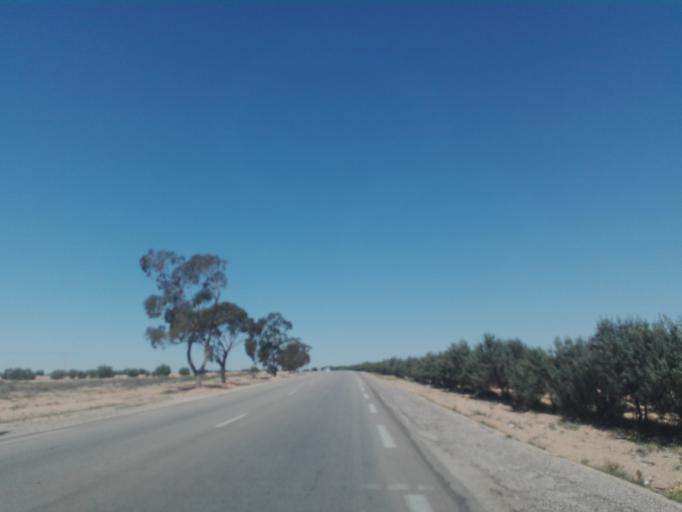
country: TN
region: Safaqis
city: Bi'r `Ali Bin Khalifah
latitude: 34.7498
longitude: 10.3489
